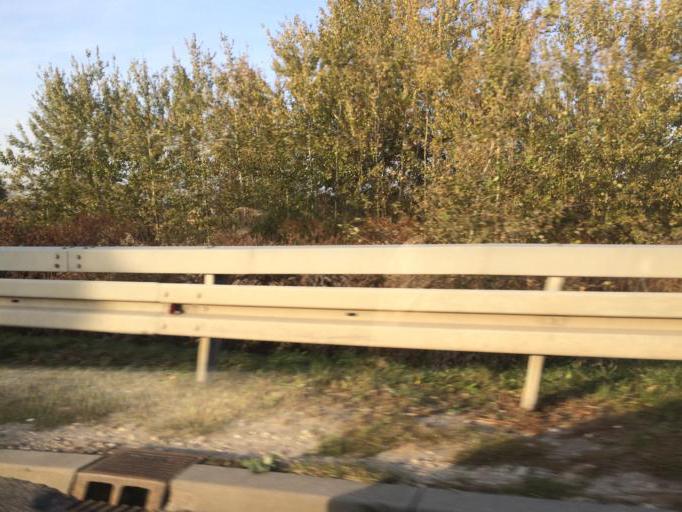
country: PL
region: Opole Voivodeship
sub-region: Powiat strzelecki
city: Strzelce Opolskie
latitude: 50.5045
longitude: 18.3259
